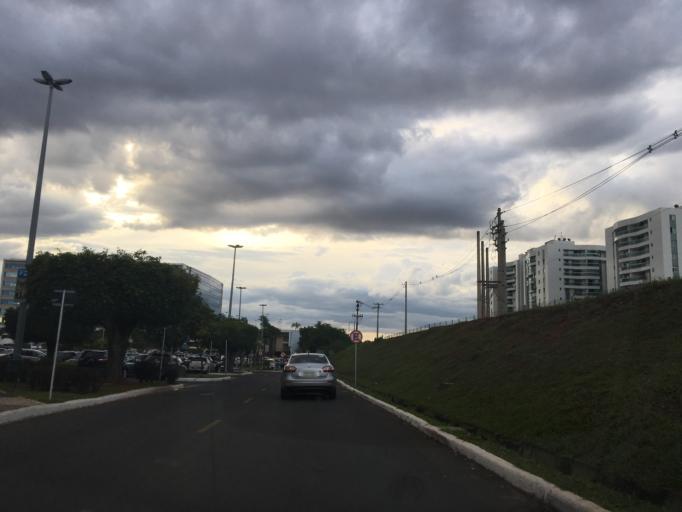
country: BR
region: Federal District
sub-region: Brasilia
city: Brasilia
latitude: -15.8321
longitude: -47.9553
